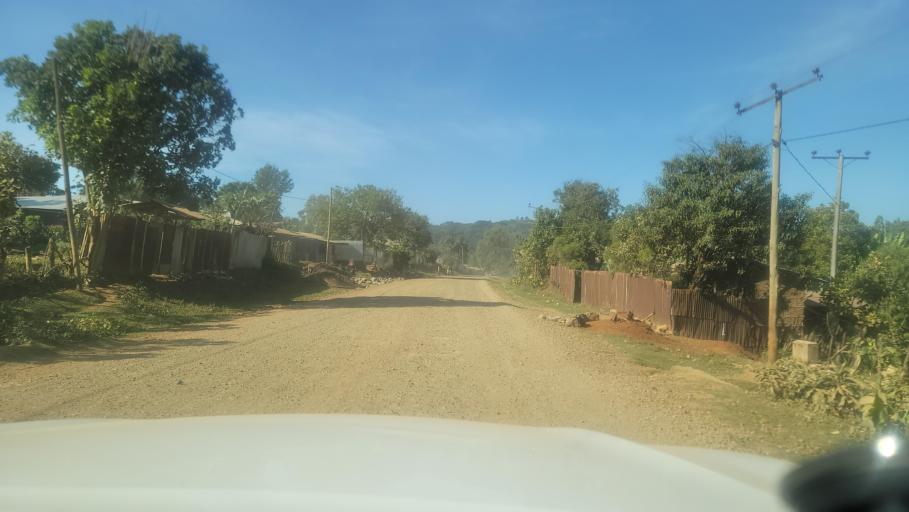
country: ET
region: Oromiya
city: Agaro
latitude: 7.8153
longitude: 36.5162
